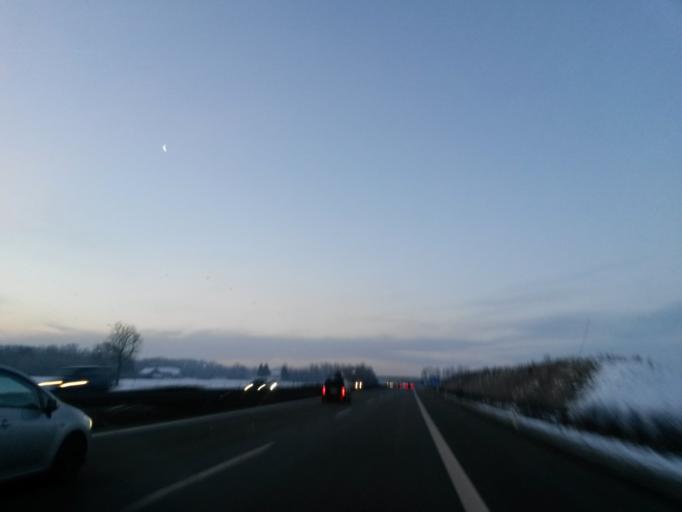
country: DE
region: Bavaria
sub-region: Swabia
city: Heimertingen
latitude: 48.0500
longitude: 10.1363
